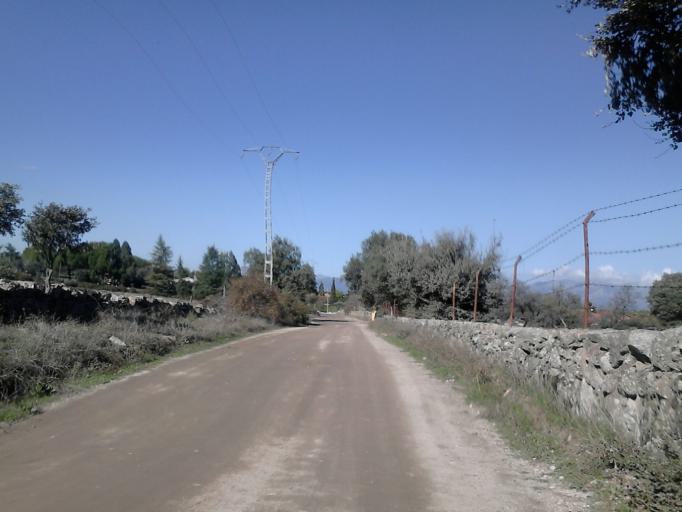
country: ES
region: Madrid
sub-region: Provincia de Madrid
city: Galapagar
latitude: 40.5651
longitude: -3.9956
